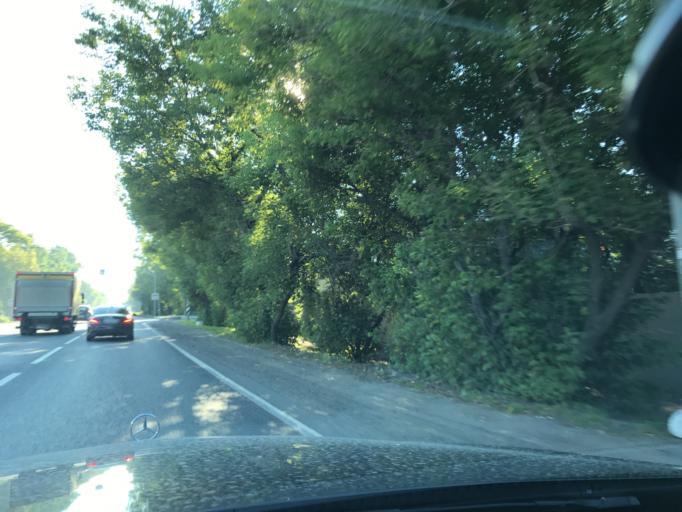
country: RU
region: Moskovskaya
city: Balashikha
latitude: 55.8307
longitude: 37.9230
